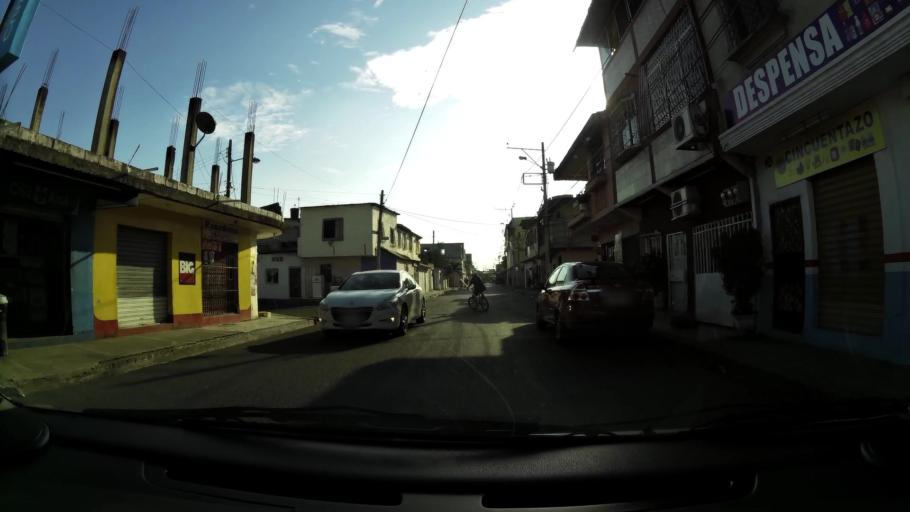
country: EC
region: Guayas
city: Guayaquil
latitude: -2.2248
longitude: -79.9079
